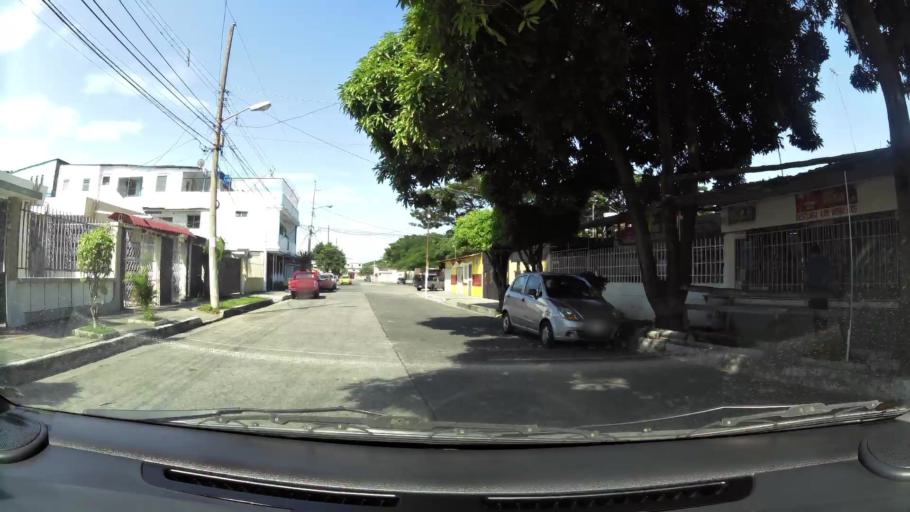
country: EC
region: Guayas
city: Guayaquil
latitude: -2.2268
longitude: -79.8966
